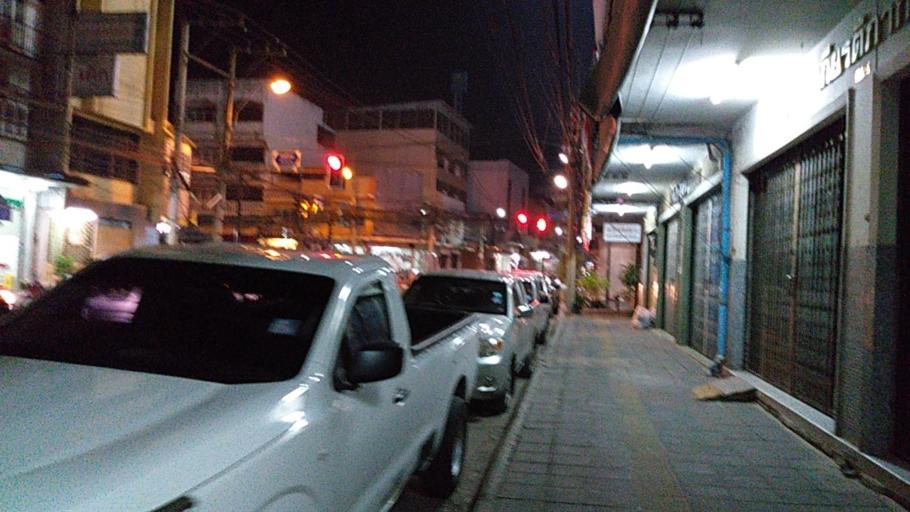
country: TH
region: Nakhon Ratchasima
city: Nakhon Ratchasima
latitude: 14.9750
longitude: 102.0953
